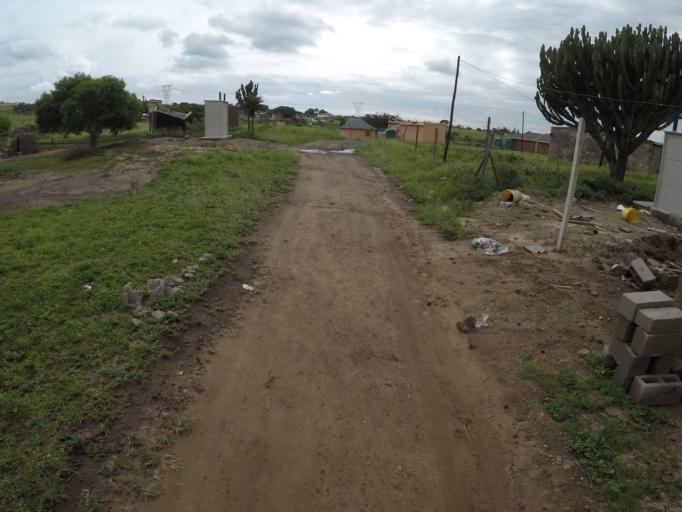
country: ZA
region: KwaZulu-Natal
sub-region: uThungulu District Municipality
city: Empangeni
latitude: -28.7110
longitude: 31.8620
